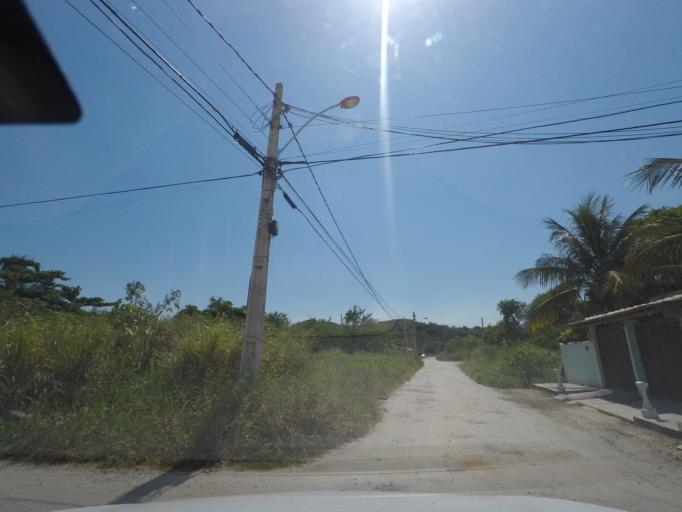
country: BR
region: Rio de Janeiro
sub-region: Marica
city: Marica
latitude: -22.9525
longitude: -42.9630
